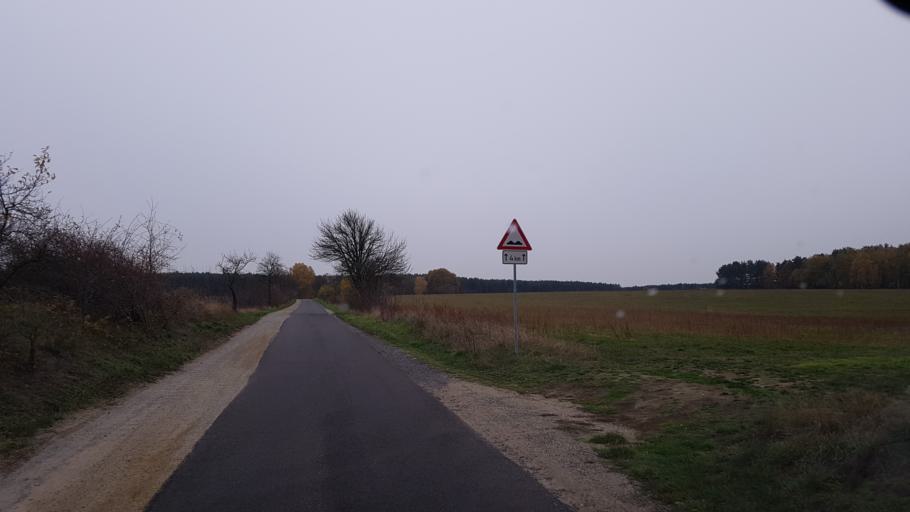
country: DE
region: Brandenburg
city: Crinitz
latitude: 51.7346
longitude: 13.7617
